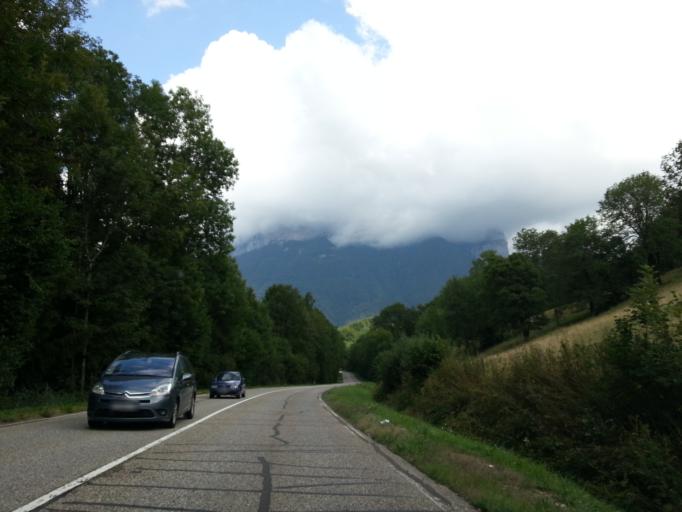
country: FR
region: Rhone-Alpes
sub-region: Departement de la Haute-Savoie
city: Dingy-Saint-Clair
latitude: 45.8820
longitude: 6.2212
